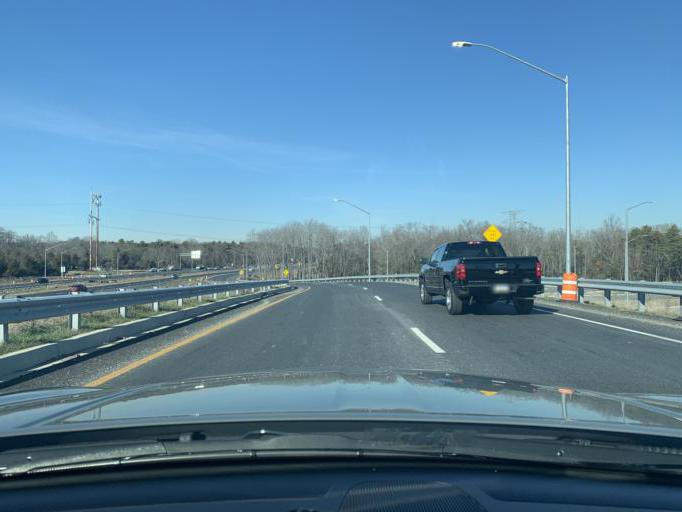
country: US
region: Maryland
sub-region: Prince George's County
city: Brandywine
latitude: 38.7055
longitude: -76.8763
